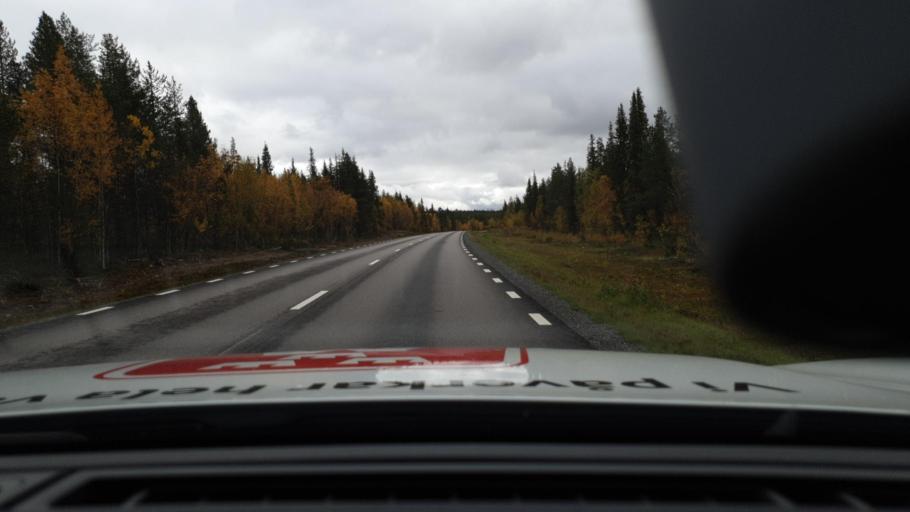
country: SE
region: Norrbotten
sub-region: Gallivare Kommun
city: Malmberget
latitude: 67.6092
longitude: 21.1125
